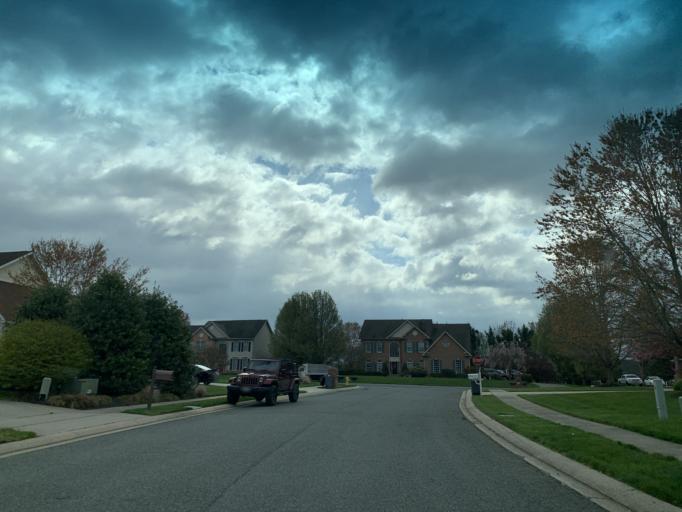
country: US
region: Maryland
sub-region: Harford County
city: South Bel Air
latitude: 39.5566
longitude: -76.3087
